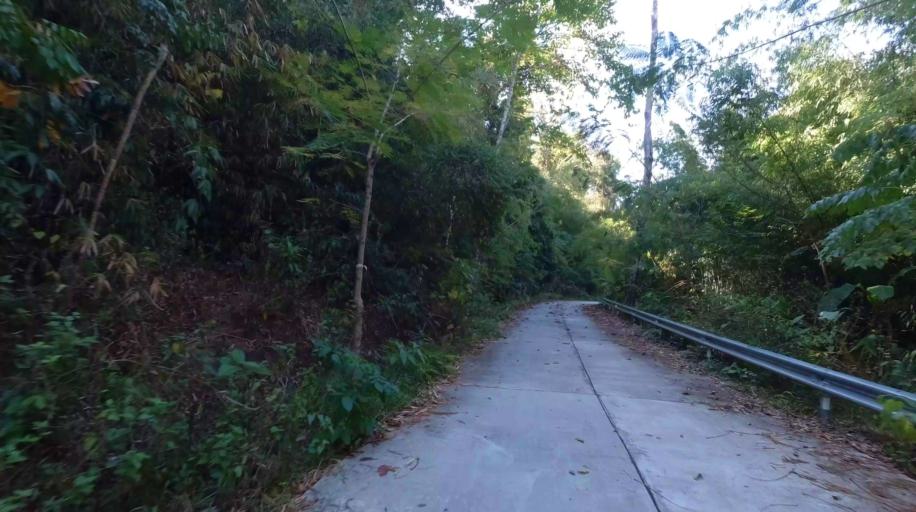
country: TH
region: Trat
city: Ko Kut
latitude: 11.6275
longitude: 102.5572
